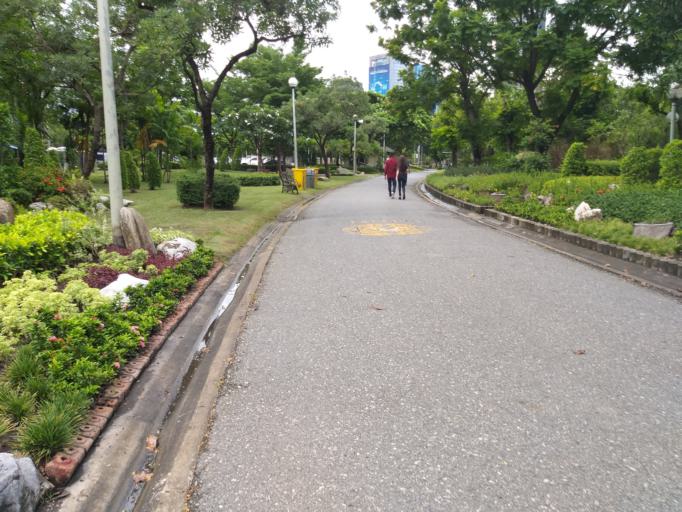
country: TH
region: Bangkok
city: Bang Sue
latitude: 13.8038
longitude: 100.5525
